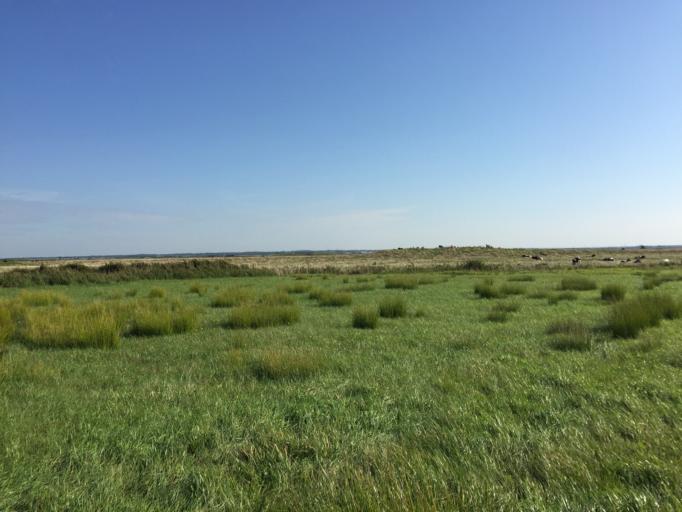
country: DK
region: South Denmark
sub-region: Tonder Kommune
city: Sherrebek
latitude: 55.1327
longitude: 8.6956
